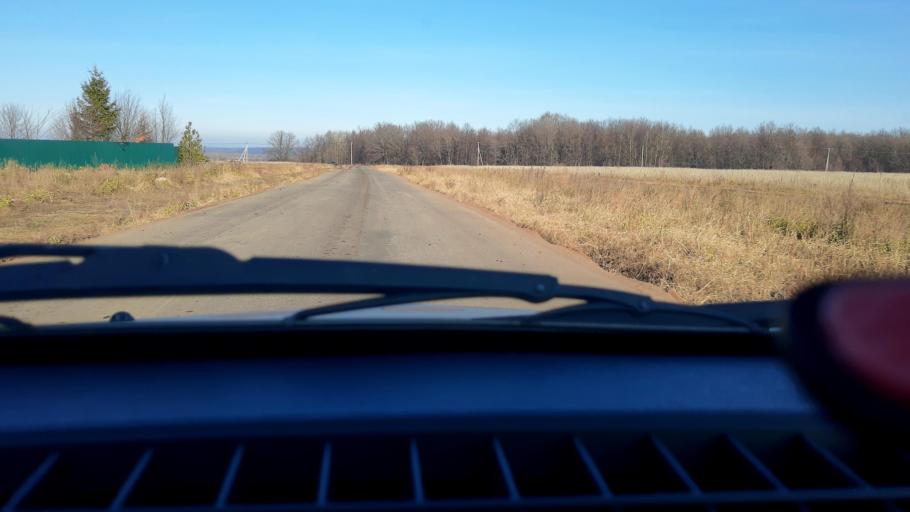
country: RU
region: Bashkortostan
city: Kabakovo
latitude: 54.6195
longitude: 56.1533
